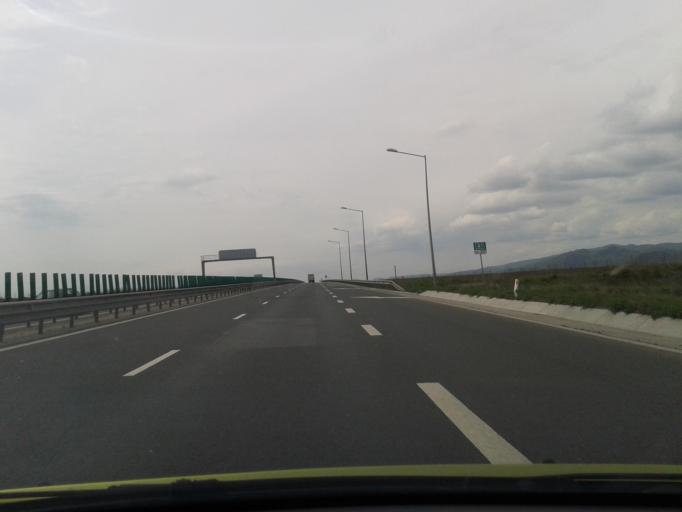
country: RO
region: Alba
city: Vurpar
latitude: 45.9641
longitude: 23.4659
